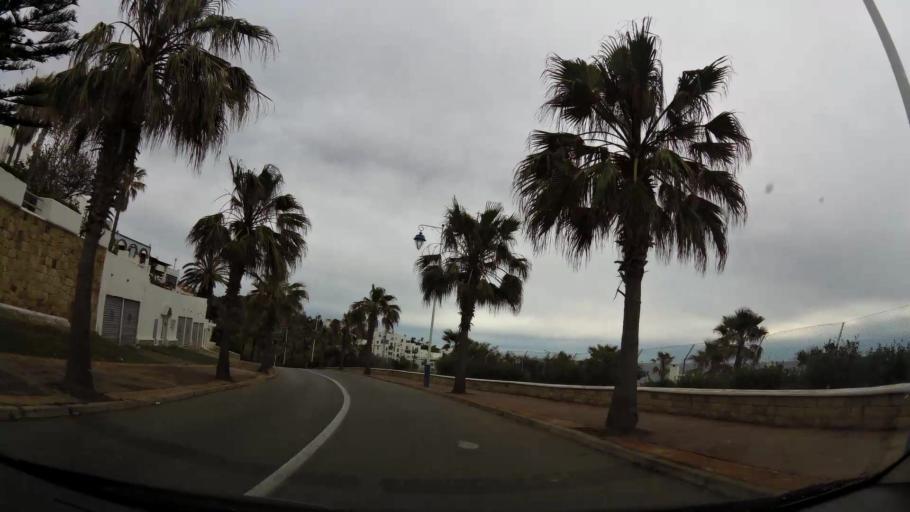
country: MA
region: Tanger-Tetouan
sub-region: Tetouan
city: Martil
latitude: 35.6655
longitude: -5.2883
